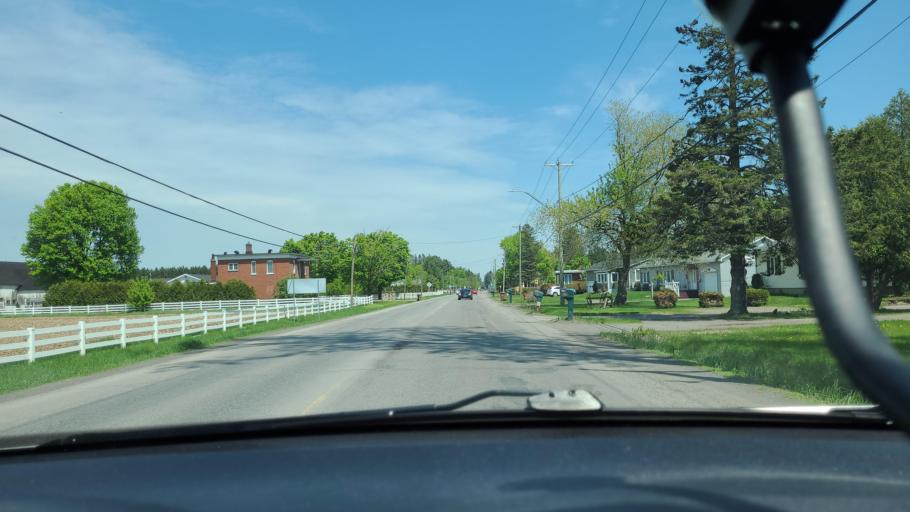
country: CA
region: Quebec
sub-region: Laurentides
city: Lachute
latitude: 45.6625
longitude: -74.3054
